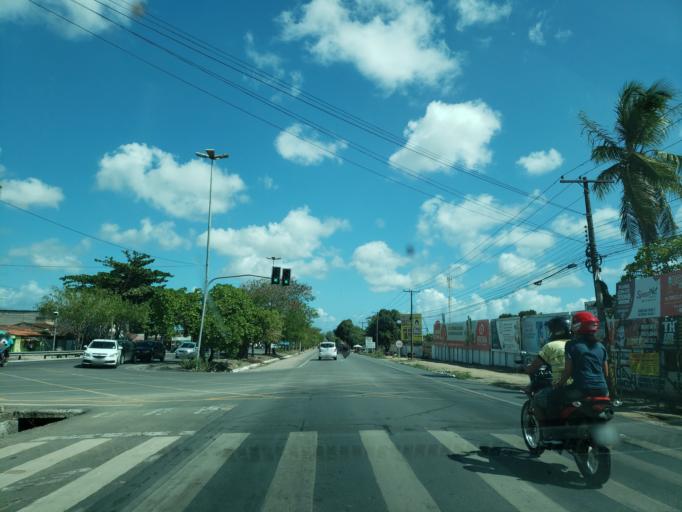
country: BR
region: Alagoas
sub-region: Satuba
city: Satuba
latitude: -9.5404
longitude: -35.7915
